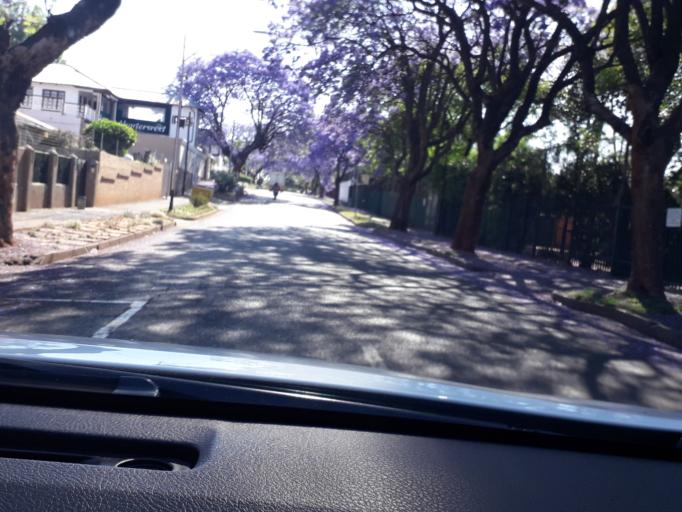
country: ZA
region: Gauteng
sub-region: City of Johannesburg Metropolitan Municipality
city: Johannesburg
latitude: -26.1779
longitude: 28.0044
